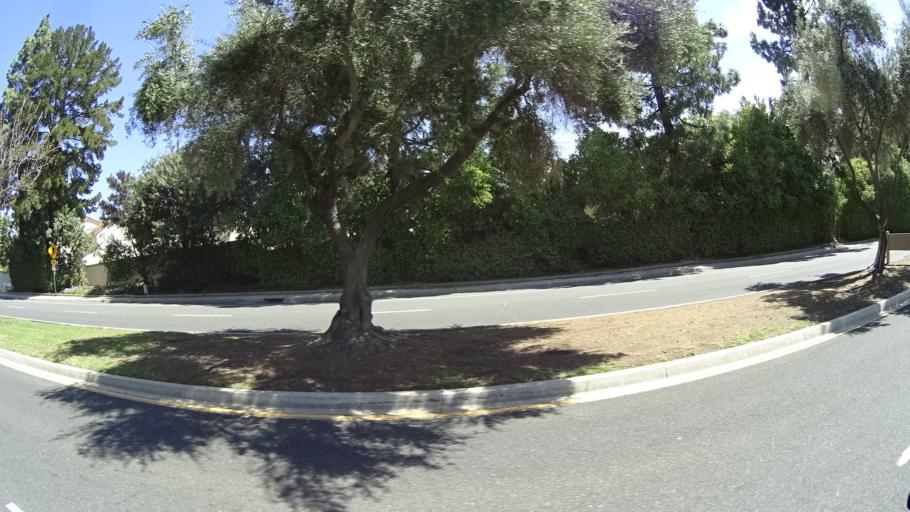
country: US
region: California
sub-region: Ventura County
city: Thousand Oaks
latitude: 34.2231
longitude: -118.8426
